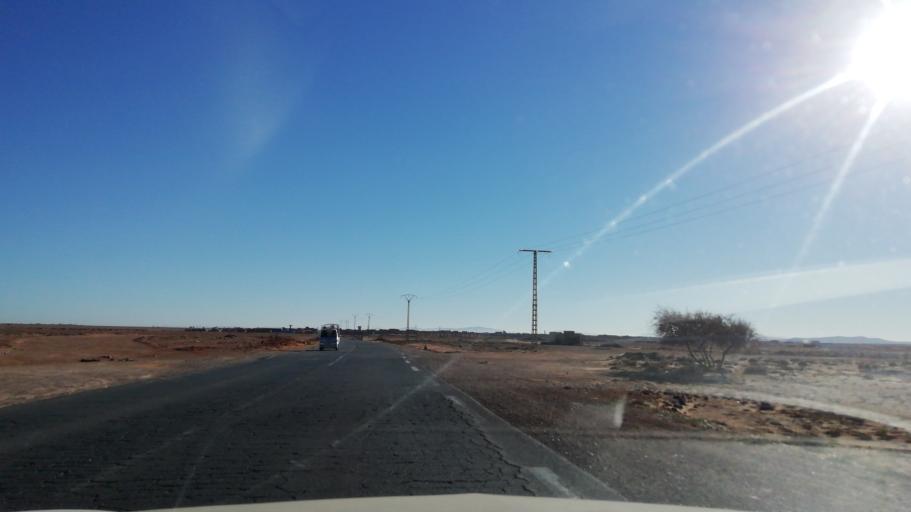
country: DZ
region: El Bayadh
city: El Bayadh
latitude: 33.8537
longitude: 0.6136
